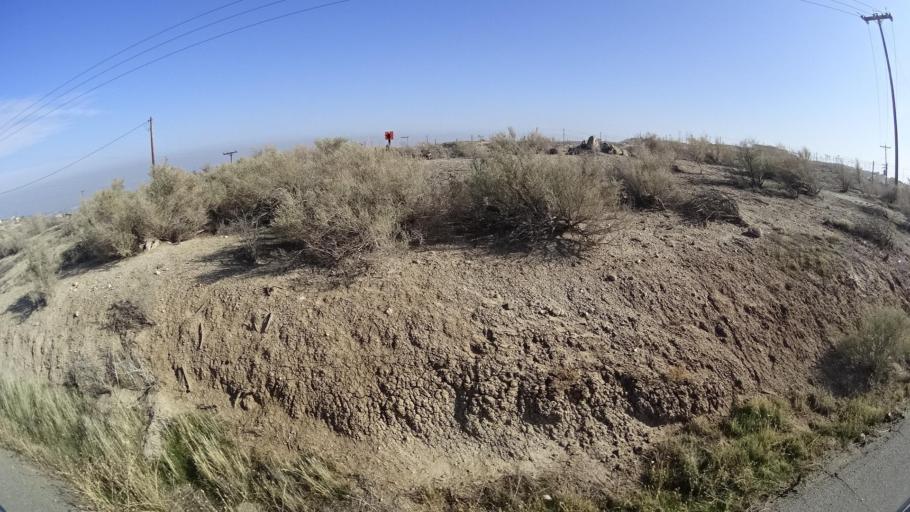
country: US
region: California
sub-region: Kern County
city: Taft Heights
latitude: 35.1175
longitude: -119.4784
